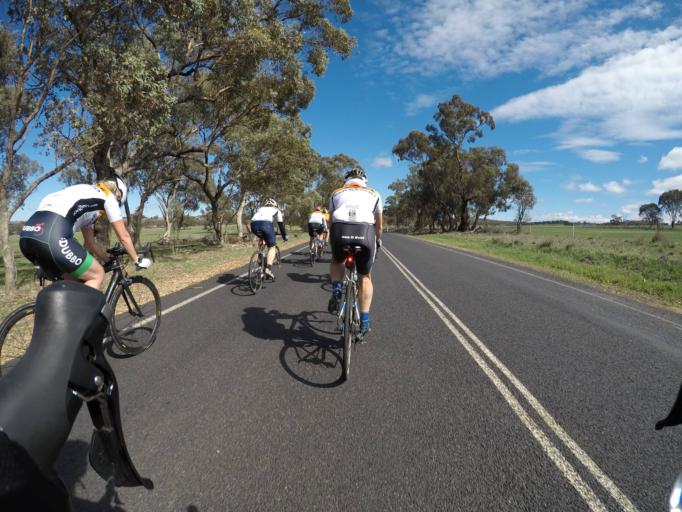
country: AU
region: New South Wales
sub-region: Parkes
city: Peak Hill
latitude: -32.7363
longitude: 148.5762
